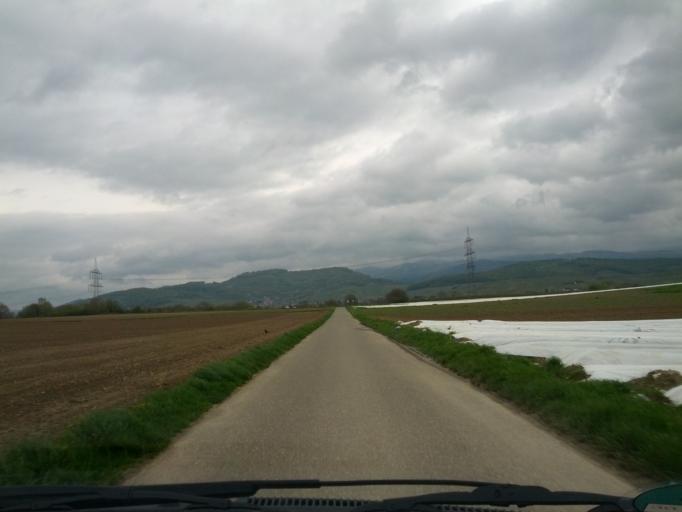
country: DE
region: Baden-Wuerttemberg
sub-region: Freiburg Region
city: Schallstadt
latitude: 47.9637
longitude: 7.7209
